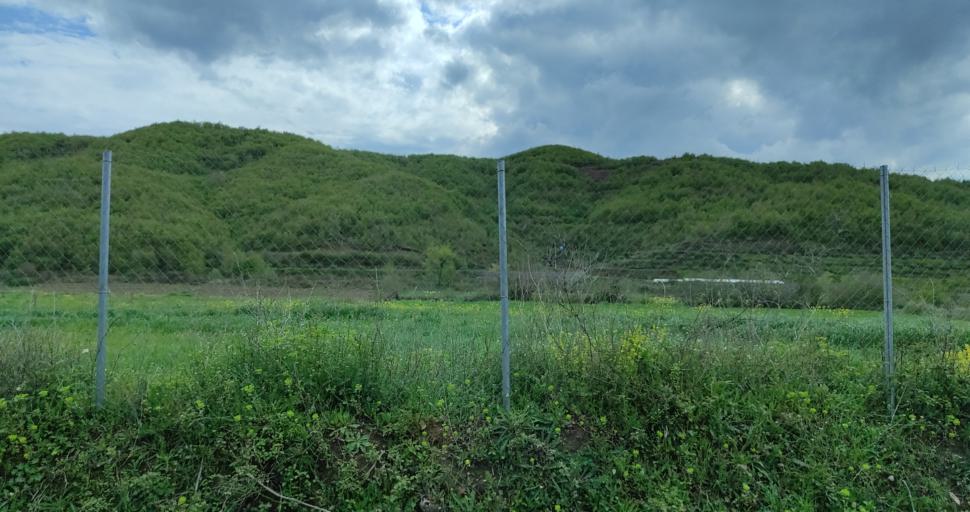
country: AL
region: Shkoder
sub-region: Rrethi i Shkodres
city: Dajc
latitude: 42.0354
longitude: 19.4035
